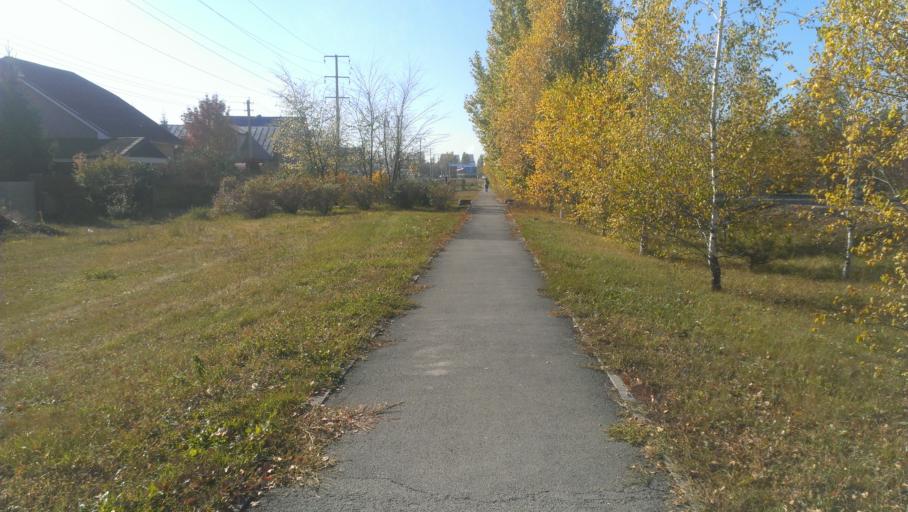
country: RU
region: Altai Krai
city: Novosilikatnyy
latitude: 53.3534
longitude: 83.6336
